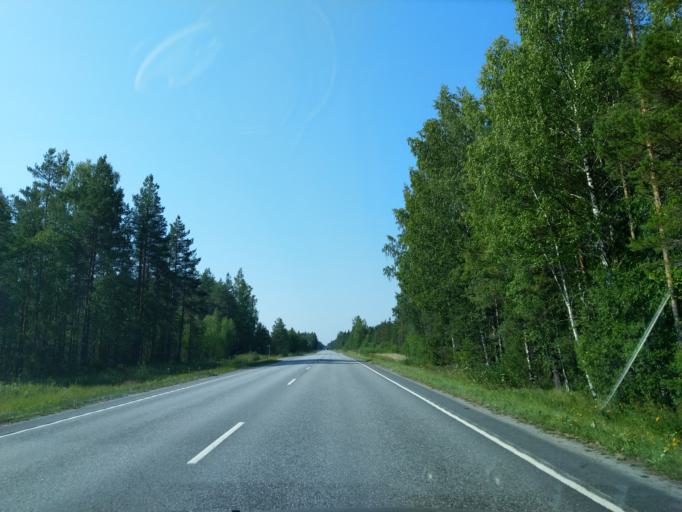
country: FI
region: Satakunta
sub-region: Pori
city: Pomarkku
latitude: 61.6809
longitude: 21.9885
